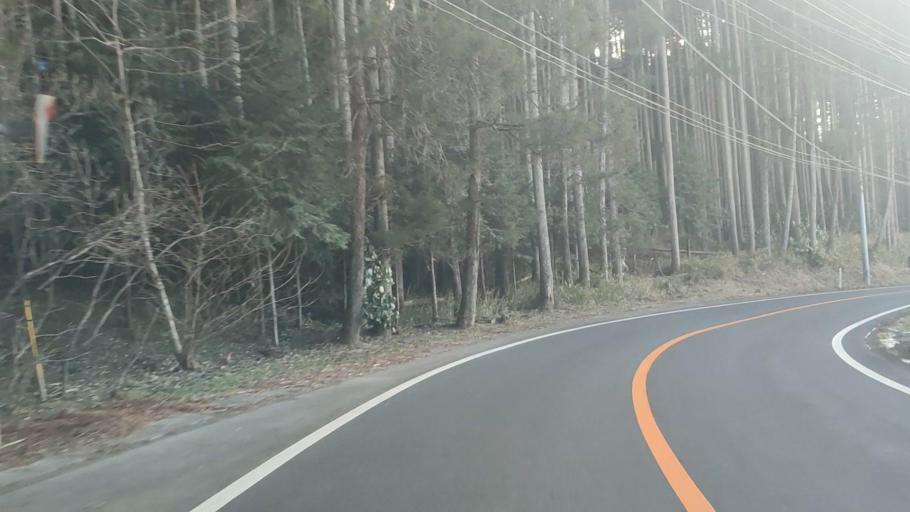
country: JP
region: Oita
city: Beppu
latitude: 33.2555
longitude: 131.3724
